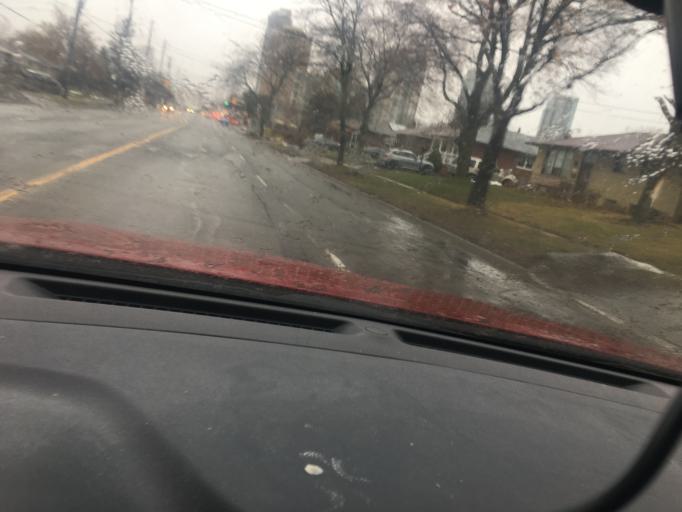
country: CA
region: Ontario
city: Scarborough
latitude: 43.7671
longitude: -79.2603
